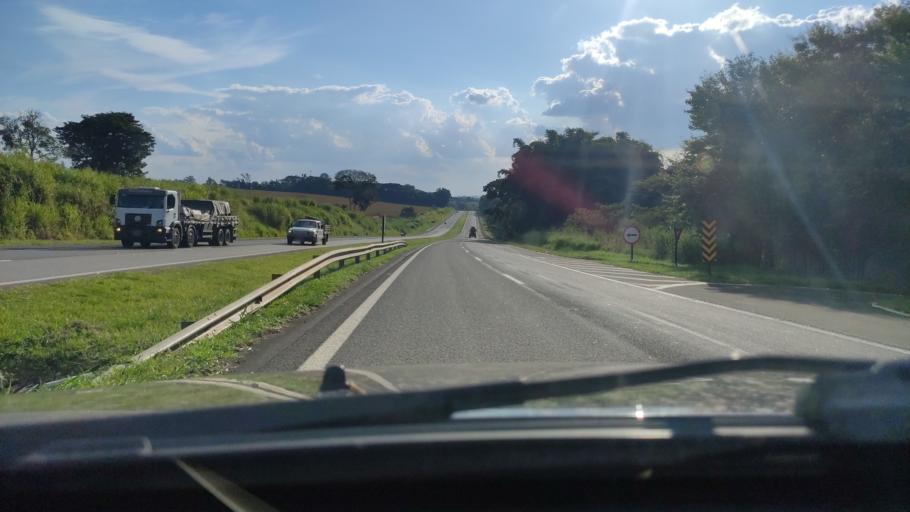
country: BR
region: Sao Paulo
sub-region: Itapira
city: Itapira
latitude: -22.4533
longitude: -46.8603
